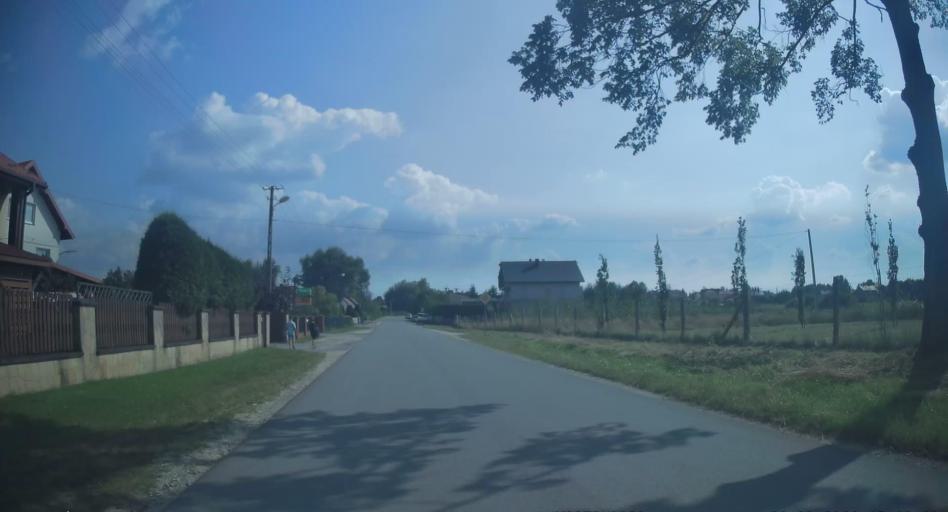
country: PL
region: Swietokrzyskie
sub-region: Powiat konecki
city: Radoszyce
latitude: 51.0819
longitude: 20.2578
